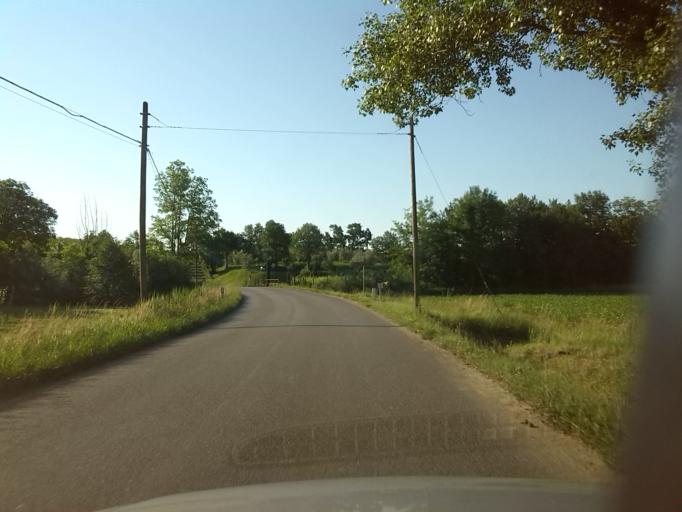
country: IT
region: Friuli Venezia Giulia
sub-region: Provincia di Udine
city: Prepotto
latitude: 46.0546
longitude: 13.4602
